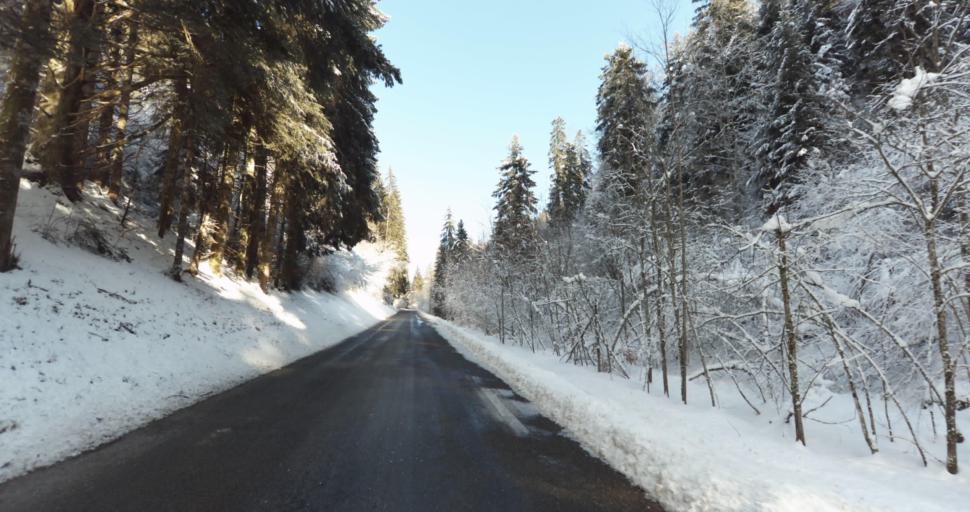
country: FR
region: Rhone-Alpes
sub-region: Departement de l'Ain
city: Nantua
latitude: 46.1719
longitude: 5.6399
